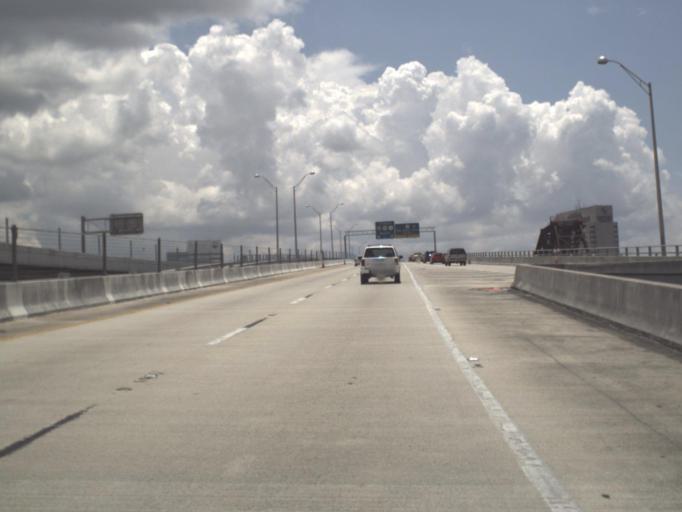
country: US
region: Florida
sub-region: Duval County
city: Jacksonville
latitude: 30.3245
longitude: -81.6662
